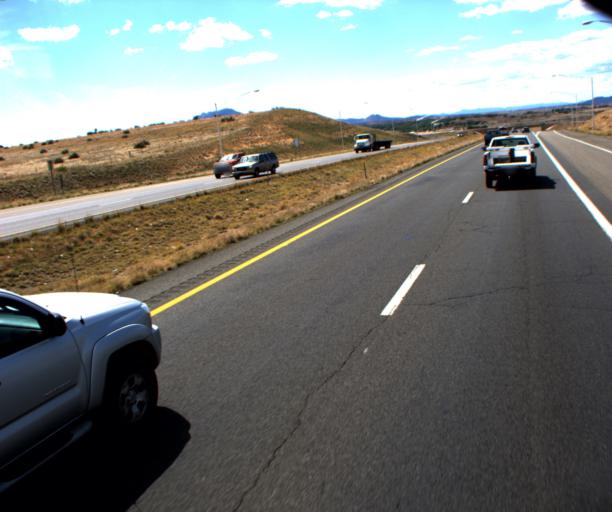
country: US
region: Arizona
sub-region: Yavapai County
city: Prescott Valley
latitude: 34.6329
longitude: -112.3914
